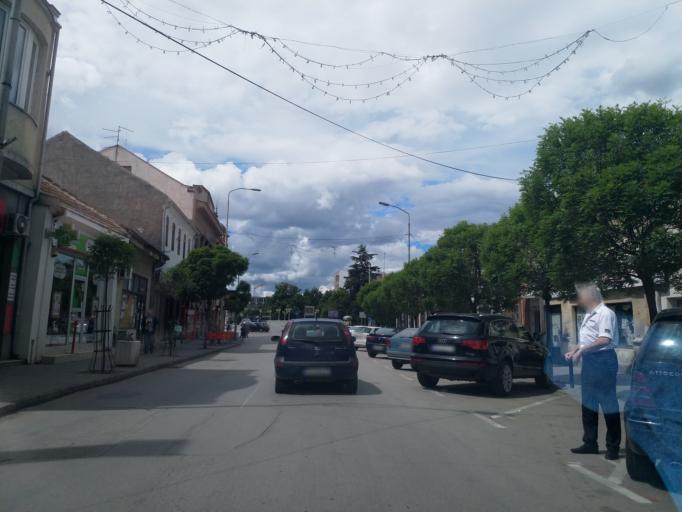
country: RS
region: Central Serbia
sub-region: Pomoravski Okrug
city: Paracin
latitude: 43.8621
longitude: 21.4108
